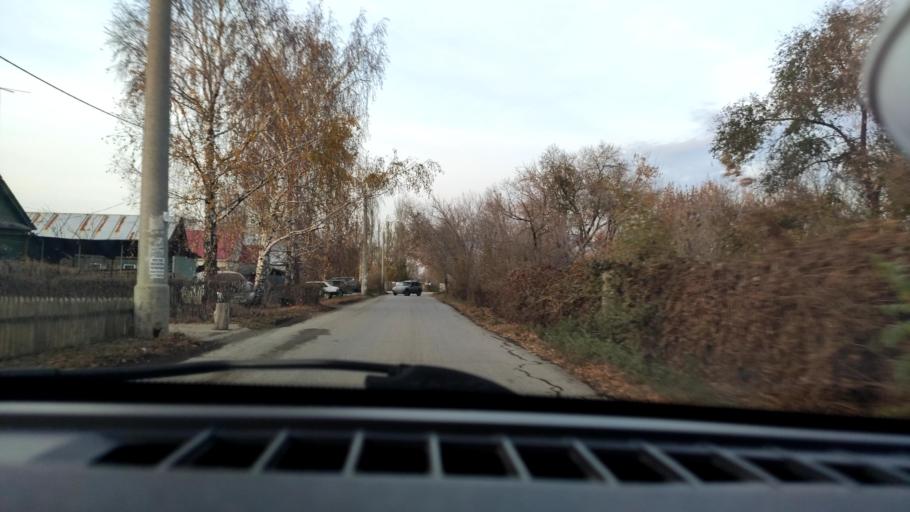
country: RU
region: Samara
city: Samara
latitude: 53.1335
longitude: 50.1356
